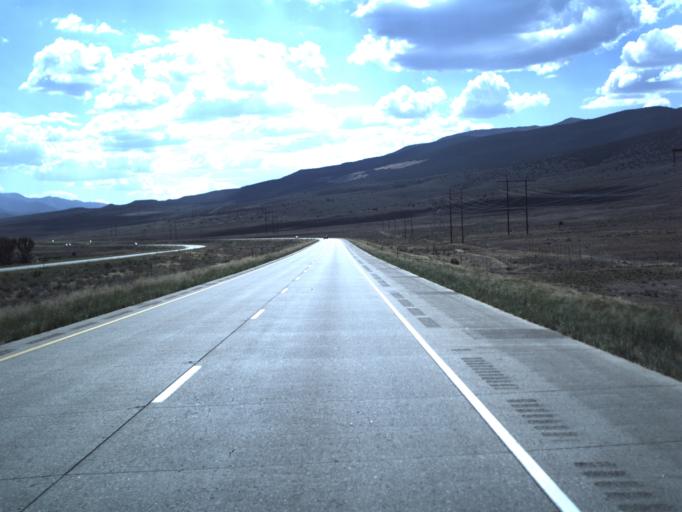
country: US
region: Utah
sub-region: Sevier County
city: Monroe
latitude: 38.6569
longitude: -112.2041
